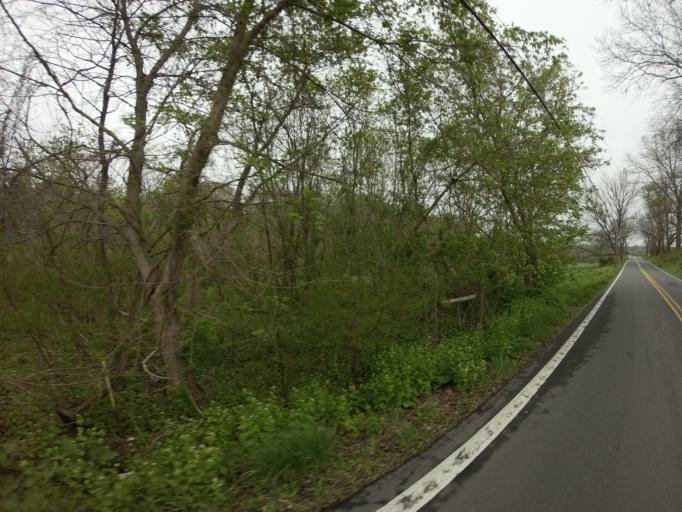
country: US
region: Maryland
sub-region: Frederick County
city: Myersville
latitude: 39.4863
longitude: -77.5340
